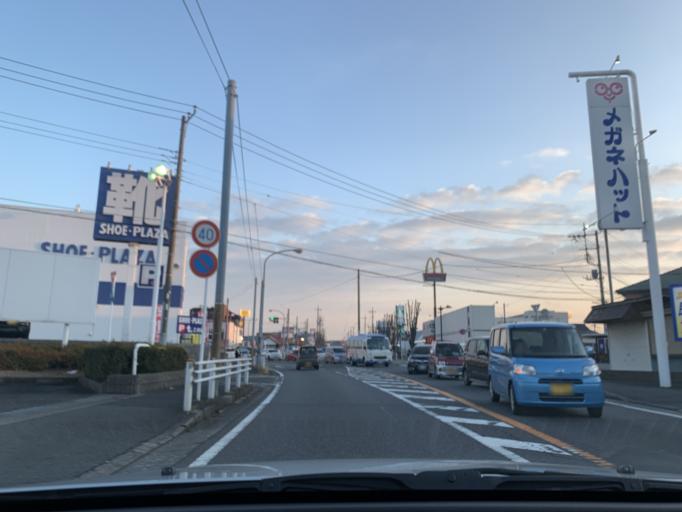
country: JP
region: Chiba
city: Matsudo
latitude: 35.7653
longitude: 139.9119
